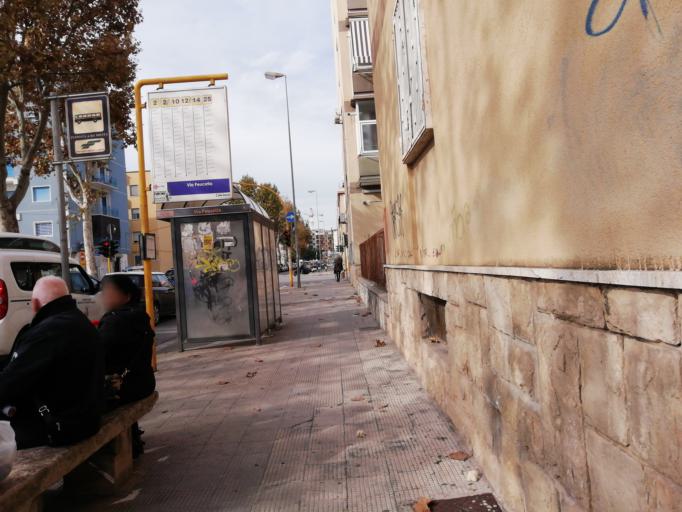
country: IT
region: Apulia
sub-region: Provincia di Bari
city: Bari
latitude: 41.1150
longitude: 16.8880
